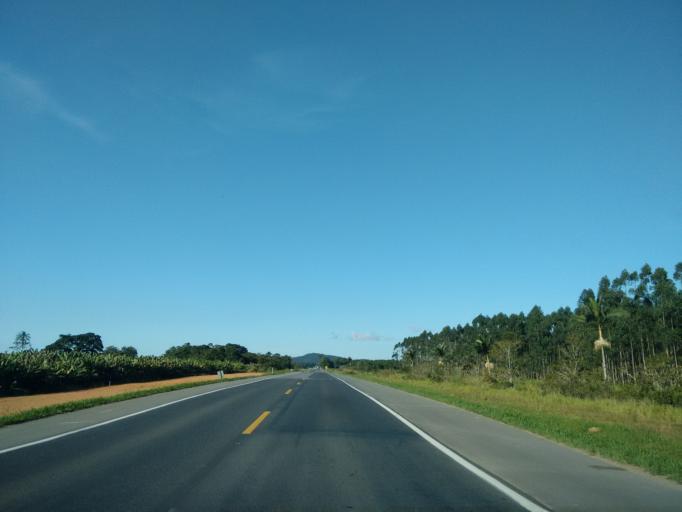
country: BR
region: Santa Catarina
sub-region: Guaramirim
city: Guaramirim
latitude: -26.4503
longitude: -48.8623
